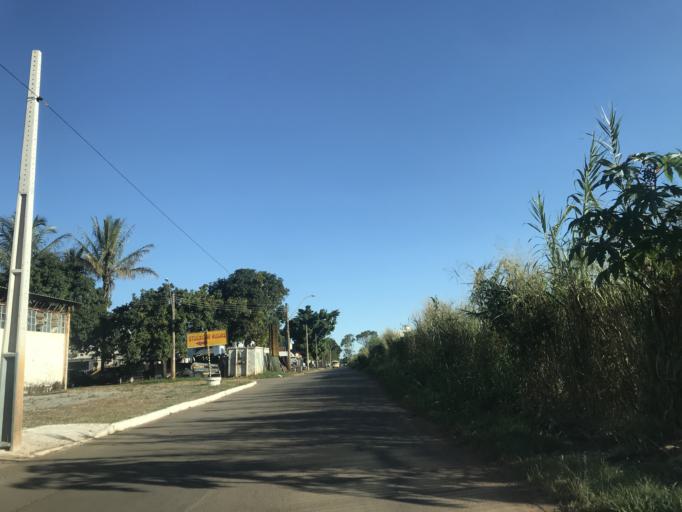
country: BR
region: Federal District
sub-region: Brasilia
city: Brasilia
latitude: -15.8195
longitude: -47.9577
